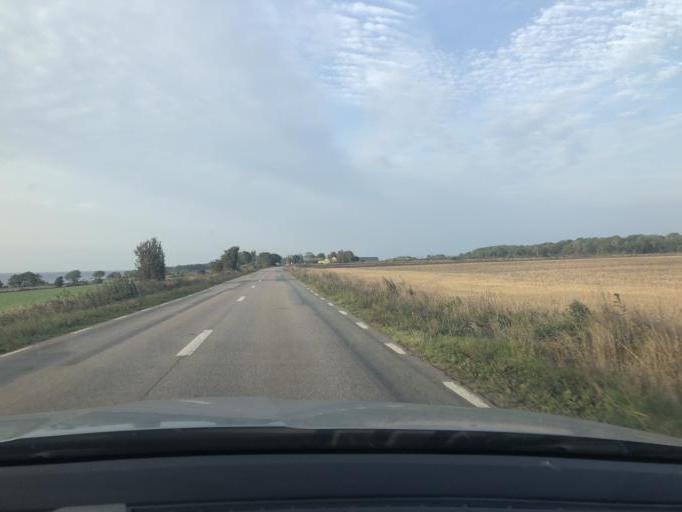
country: SE
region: Kalmar
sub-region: Morbylanga Kommun
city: Moerbylanga
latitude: 56.3161
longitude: 16.4057
